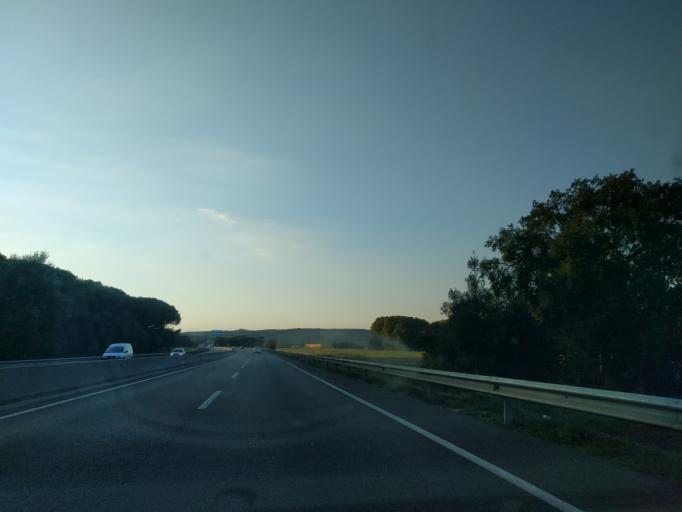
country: ES
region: Catalonia
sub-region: Provincia de Girona
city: Santa Cristina d'Aro
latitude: 41.8134
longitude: 2.9903
